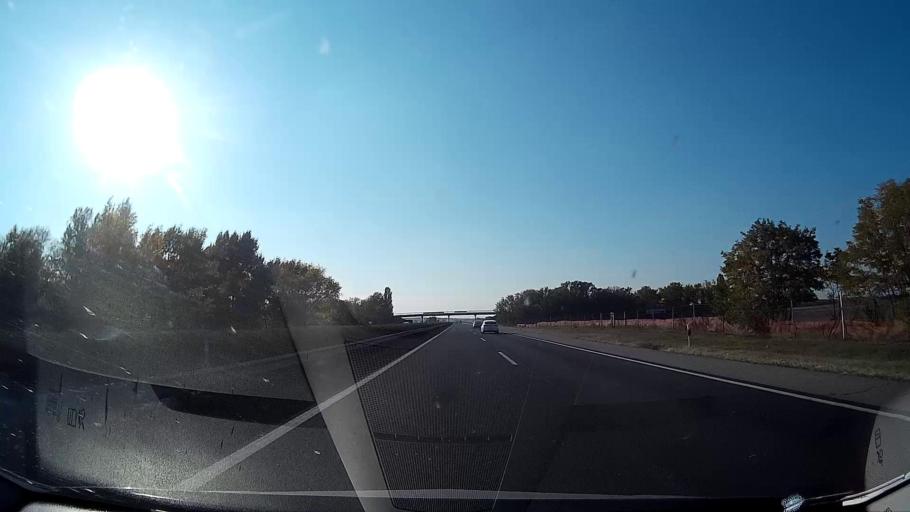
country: HU
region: Gyor-Moson-Sopron
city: Bony
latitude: 47.6850
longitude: 17.8651
